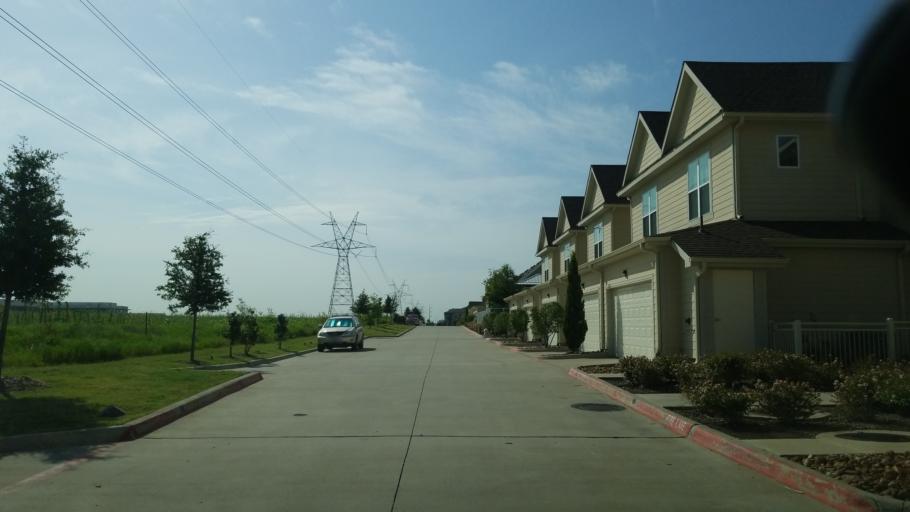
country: US
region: Texas
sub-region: Dallas County
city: Coppell
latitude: 32.9357
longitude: -96.9901
